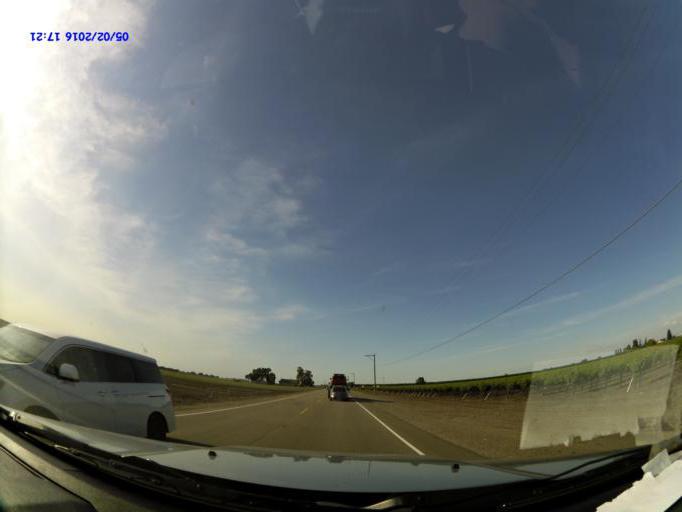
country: US
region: California
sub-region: San Joaquin County
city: Manteca
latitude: 37.8490
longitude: -121.1453
